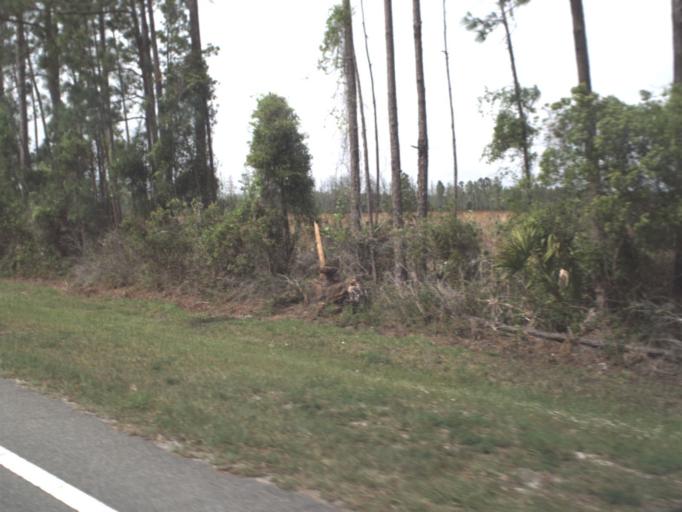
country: US
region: Florida
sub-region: Putnam County
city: Crescent City
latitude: 29.5279
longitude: -81.5124
